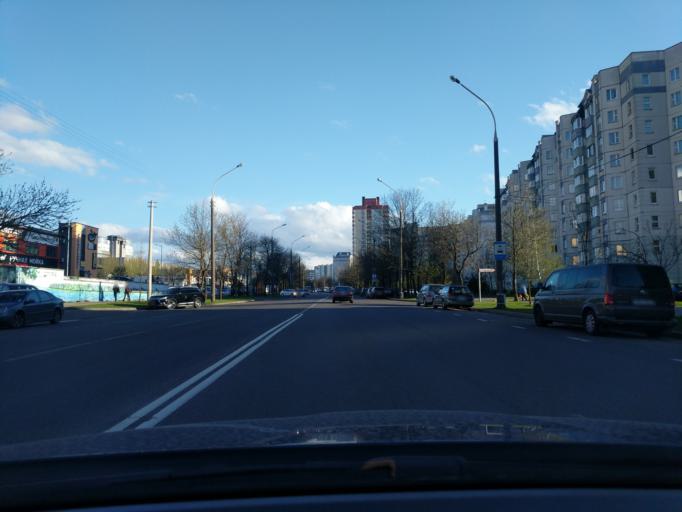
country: BY
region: Minsk
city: Novoye Medvezhino
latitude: 53.9171
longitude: 27.4496
